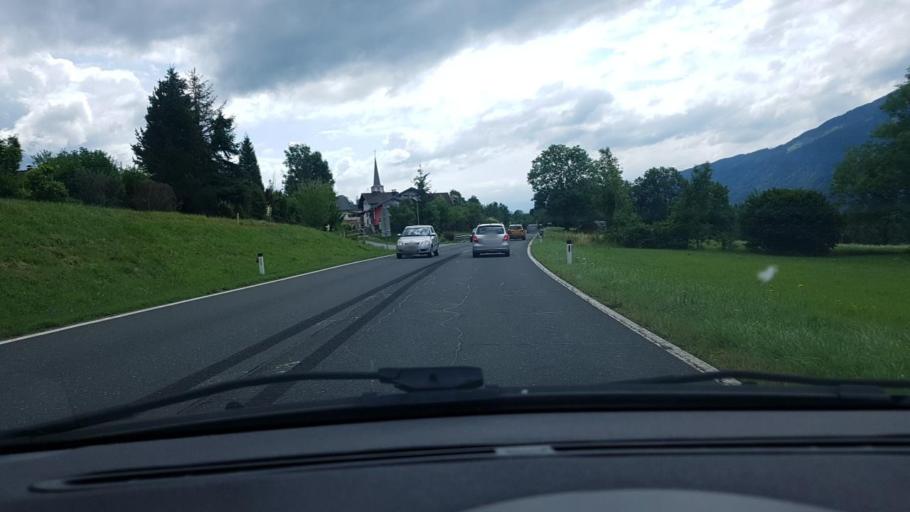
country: AT
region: Carinthia
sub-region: Politischer Bezirk Hermagor
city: Hermagor
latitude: 46.6307
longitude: 13.4677
